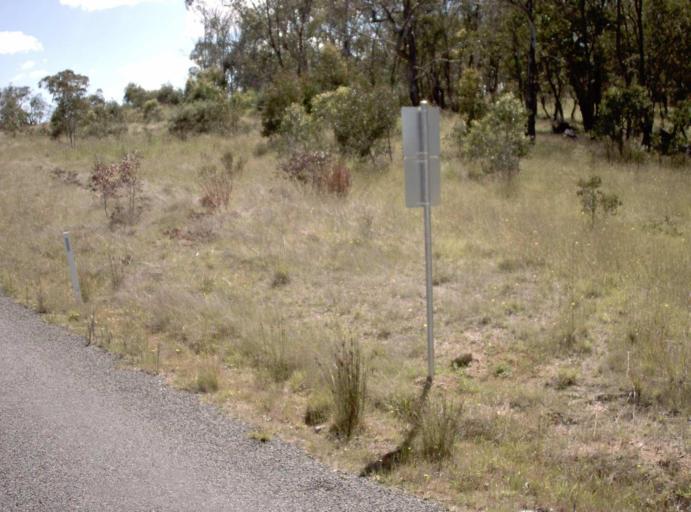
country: AU
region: New South Wales
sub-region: Bombala
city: Bombala
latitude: -37.0450
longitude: 148.8135
